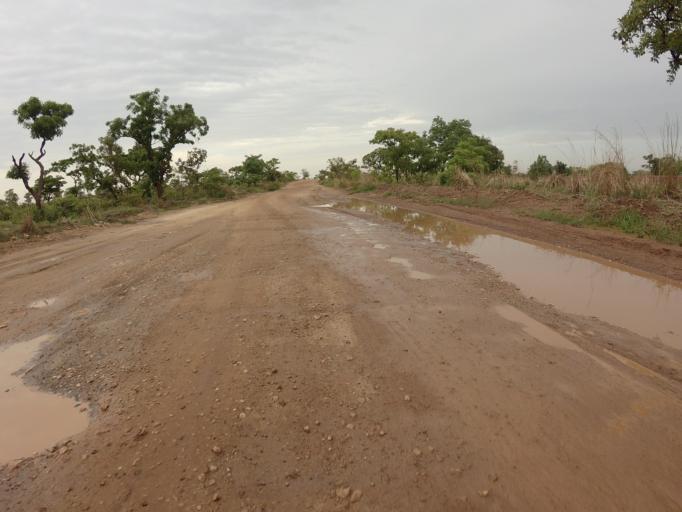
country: GH
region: Upper East
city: Bolgatanga
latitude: 10.8784
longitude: -0.6264
